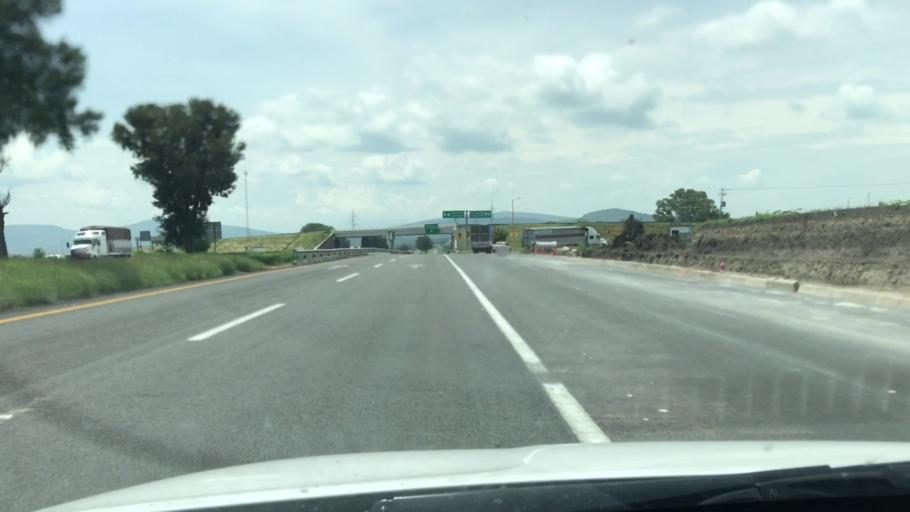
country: MX
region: Michoacan
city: Vistahermosa de Negrete
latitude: 20.2707
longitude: -102.4424
